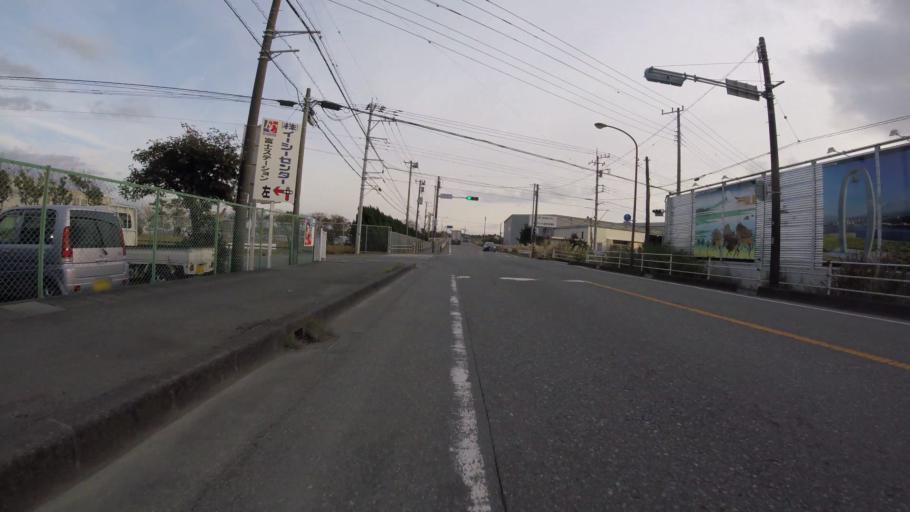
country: JP
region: Shizuoka
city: Fuji
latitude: 35.1429
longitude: 138.7211
